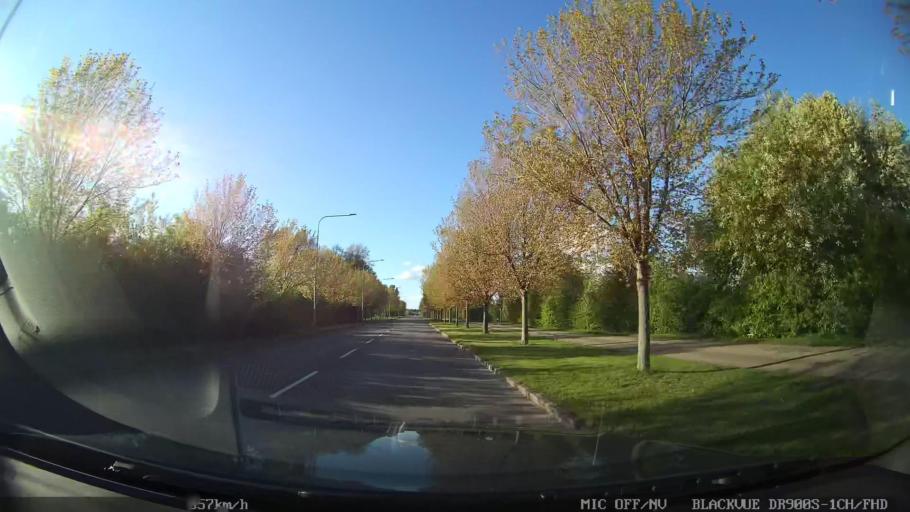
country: SE
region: Skane
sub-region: Landskrona
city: Landskrona
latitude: 55.8928
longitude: 12.8157
